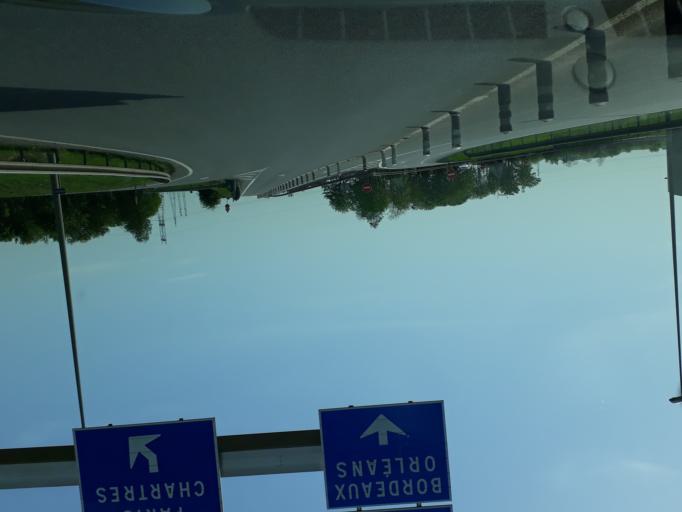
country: FR
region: Centre
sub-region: Departement du Loiret
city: Artenay
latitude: 48.0843
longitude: 1.8546
